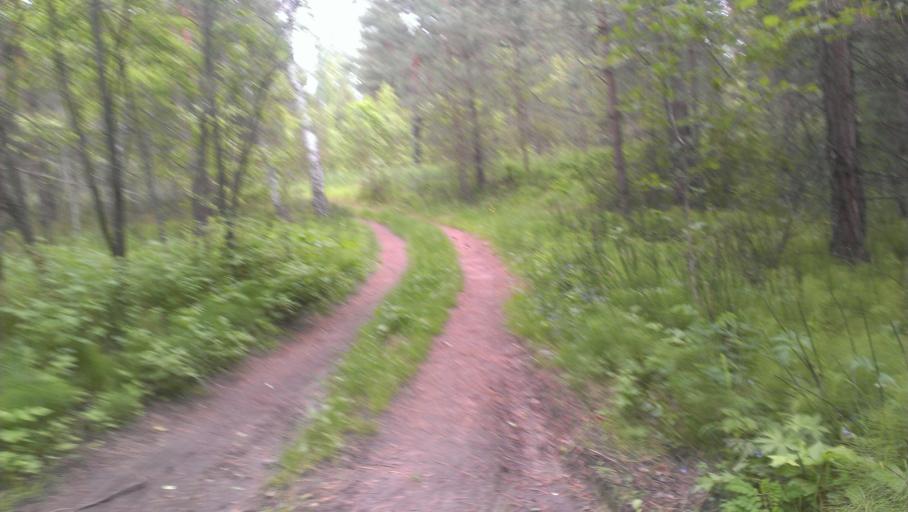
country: RU
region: Altai Krai
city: Sannikovo
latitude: 53.3493
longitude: 84.0341
